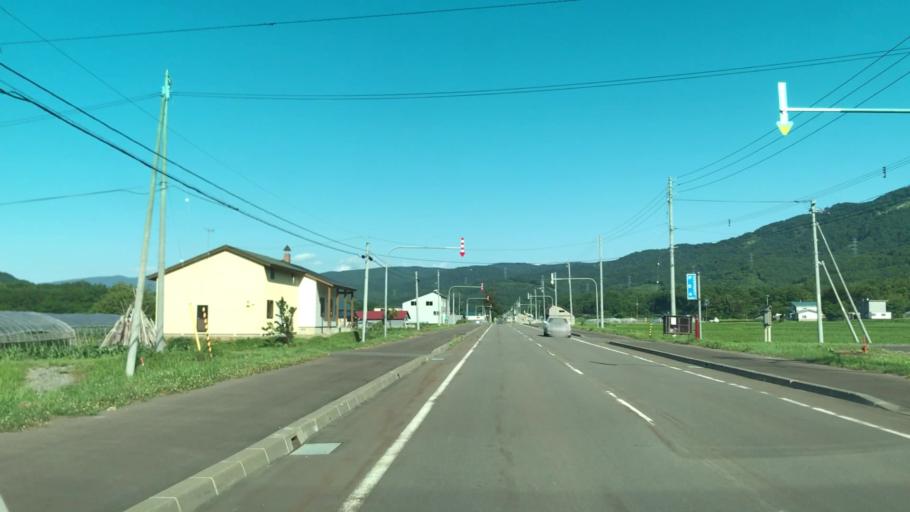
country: JP
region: Hokkaido
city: Yoichi
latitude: 43.0382
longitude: 140.7389
